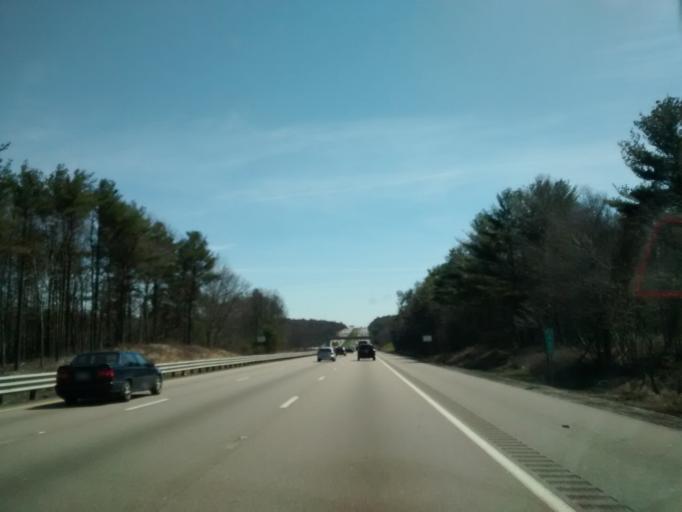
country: US
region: Massachusetts
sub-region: Norfolk County
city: Randolph
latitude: 42.1961
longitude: -71.0785
